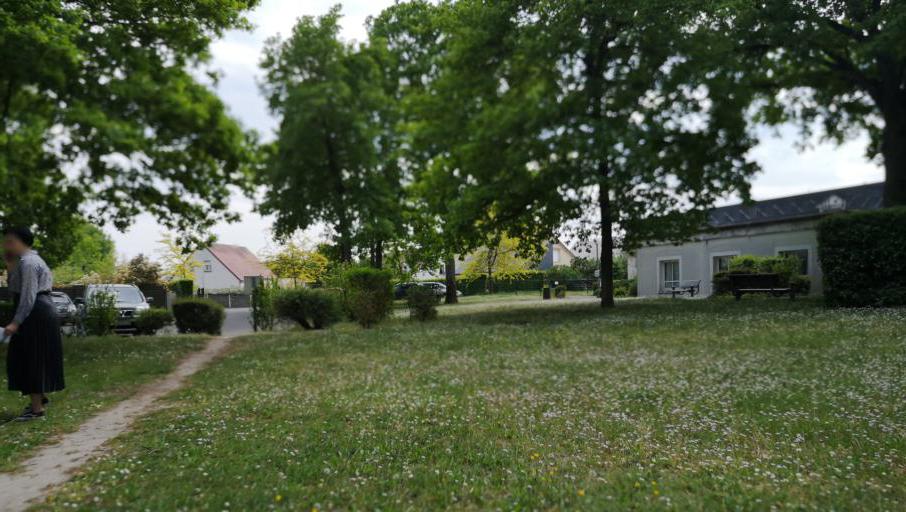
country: FR
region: Centre
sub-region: Departement du Loiret
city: Fleury-les-Aubrais
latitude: 47.9251
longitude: 1.9244
